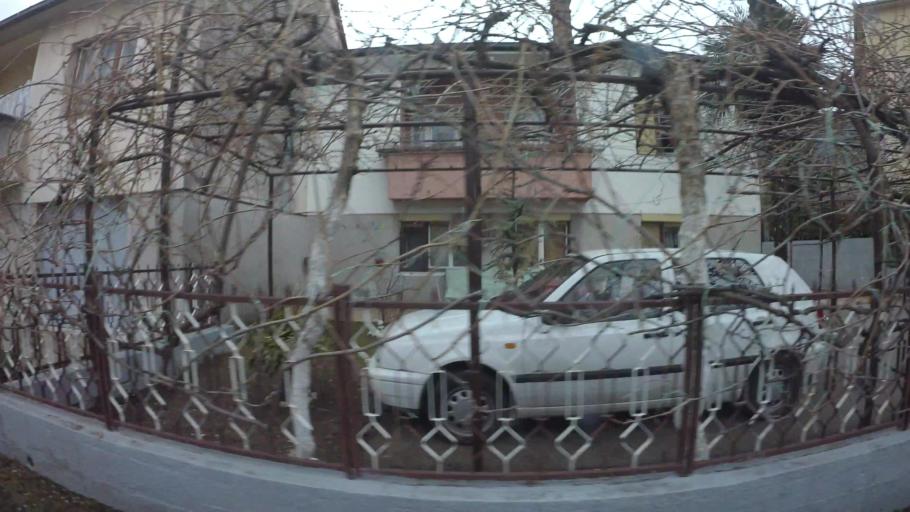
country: BA
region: Federation of Bosnia and Herzegovina
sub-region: Hercegovacko-Bosanski Kanton
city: Mostar
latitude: 43.3368
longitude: 17.7997
